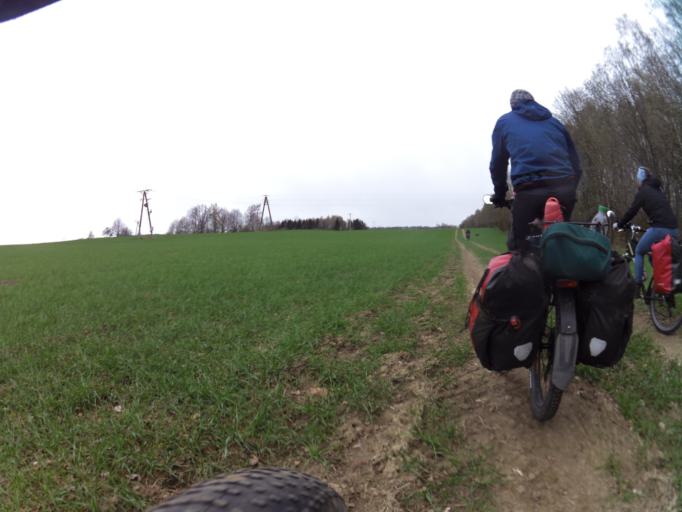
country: PL
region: West Pomeranian Voivodeship
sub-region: Powiat koszalinski
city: Polanow
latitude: 54.1168
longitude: 16.6166
